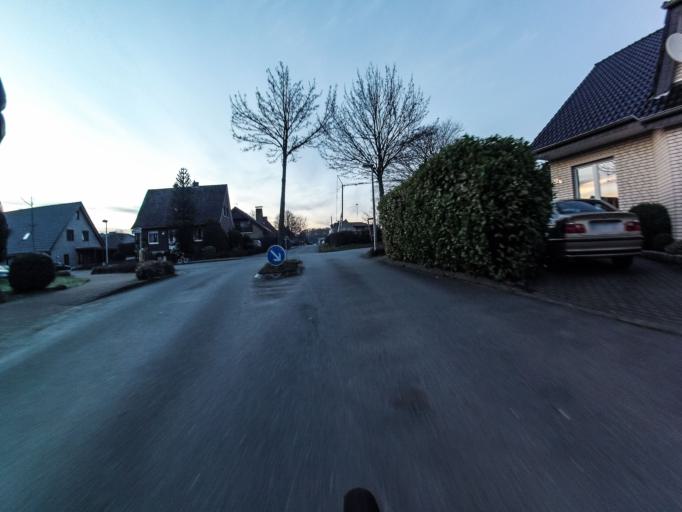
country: DE
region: North Rhine-Westphalia
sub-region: Regierungsbezirk Munster
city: Mettingen
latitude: 52.2683
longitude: 7.7921
